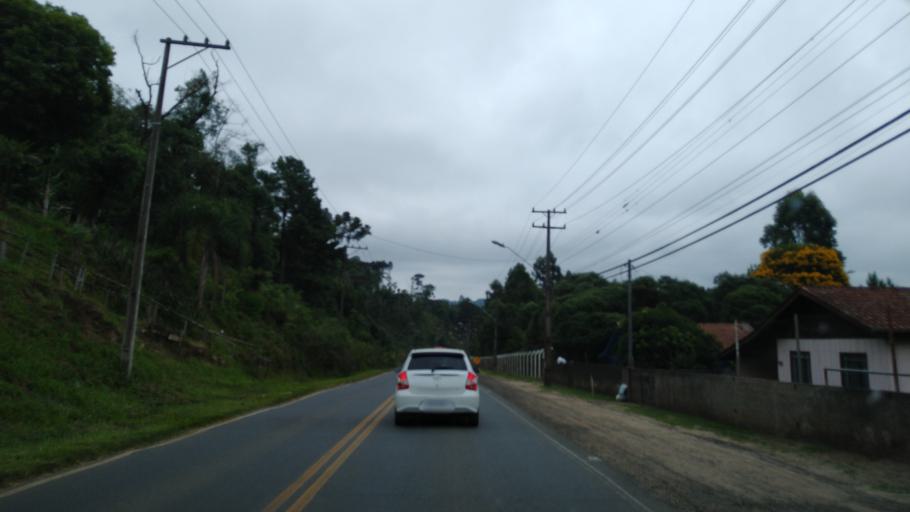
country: BR
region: Parana
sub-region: Uniao Da Vitoria
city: Uniao da Vitoria
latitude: -26.2502
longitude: -51.1190
